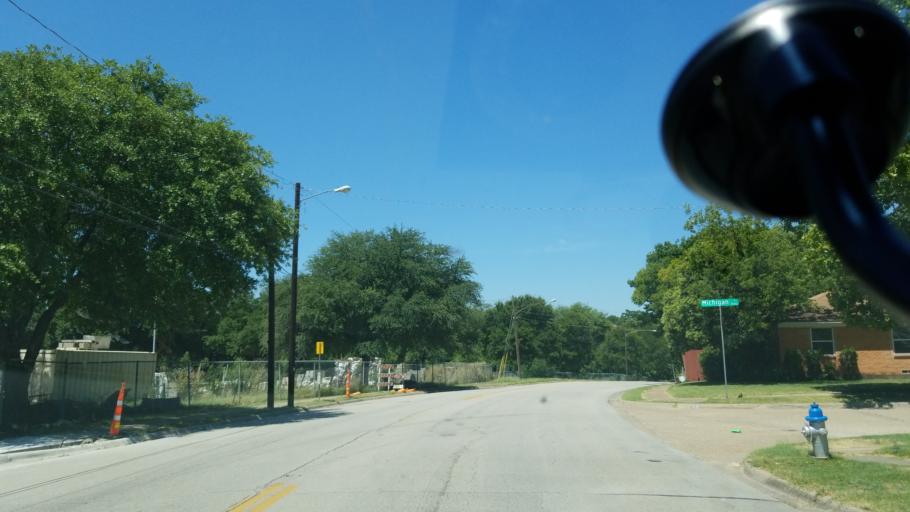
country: US
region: Texas
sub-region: Dallas County
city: Cockrell Hill
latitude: 32.7004
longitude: -96.8170
